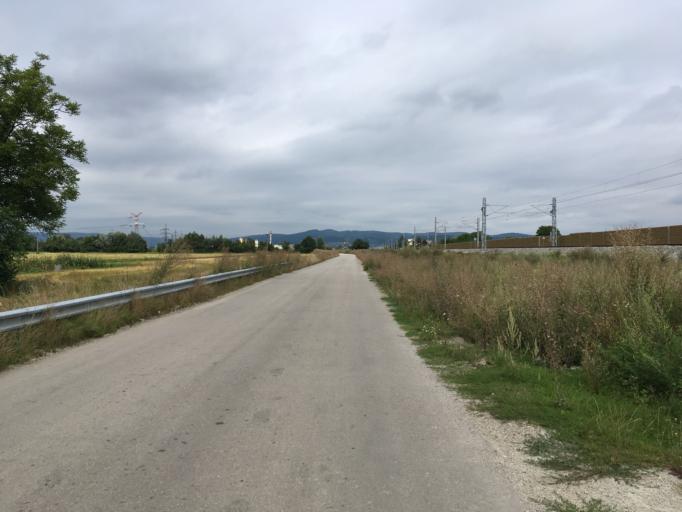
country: SK
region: Nitriansky
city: Puchov
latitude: 49.0524
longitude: 18.3084
